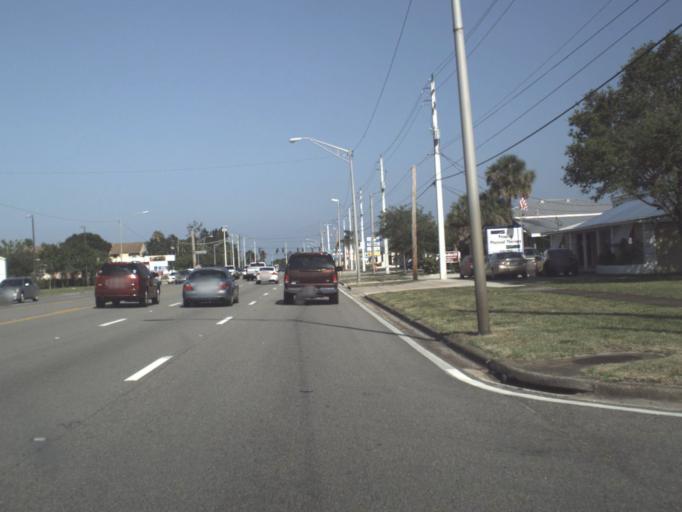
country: US
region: Florida
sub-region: Brevard County
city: Melbourne
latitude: 28.1169
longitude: -80.6256
